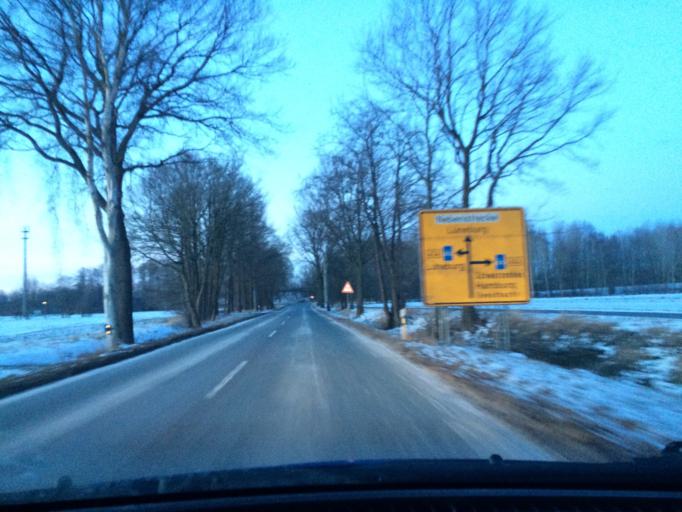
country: DE
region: Lower Saxony
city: Handorf
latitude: 53.3882
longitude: 10.3460
